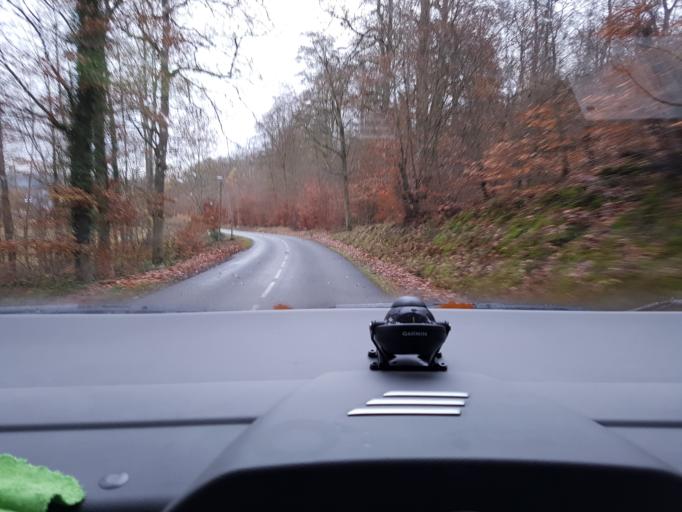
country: FR
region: Haute-Normandie
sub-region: Departement de l'Eure
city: Beaumont-le-Roger
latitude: 49.0692
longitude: 0.7710
